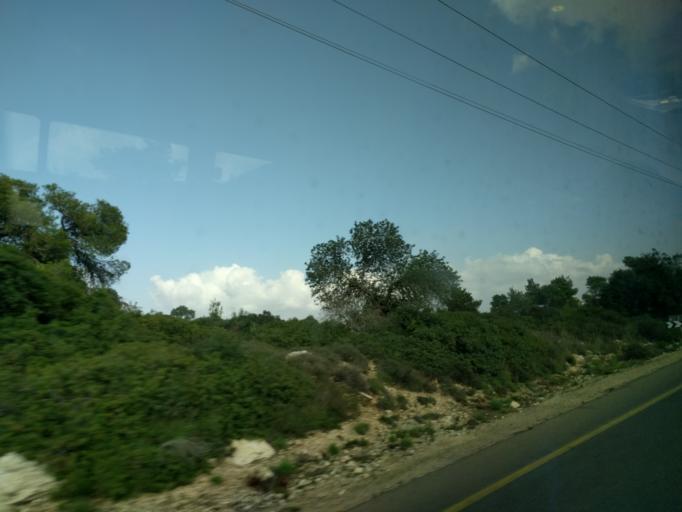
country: IL
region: Haifa
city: Nesher
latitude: 32.7349
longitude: 35.0418
